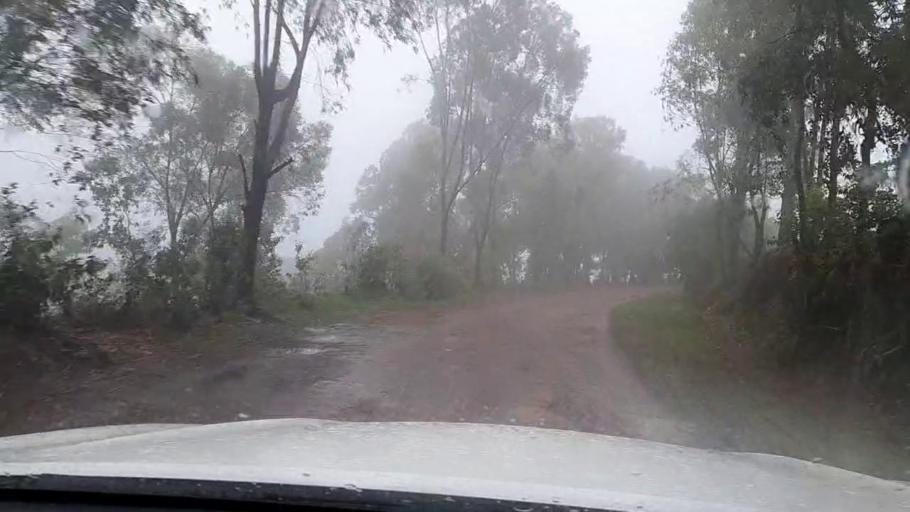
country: RW
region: Kigali
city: Kigali
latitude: -1.7750
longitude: 30.0004
